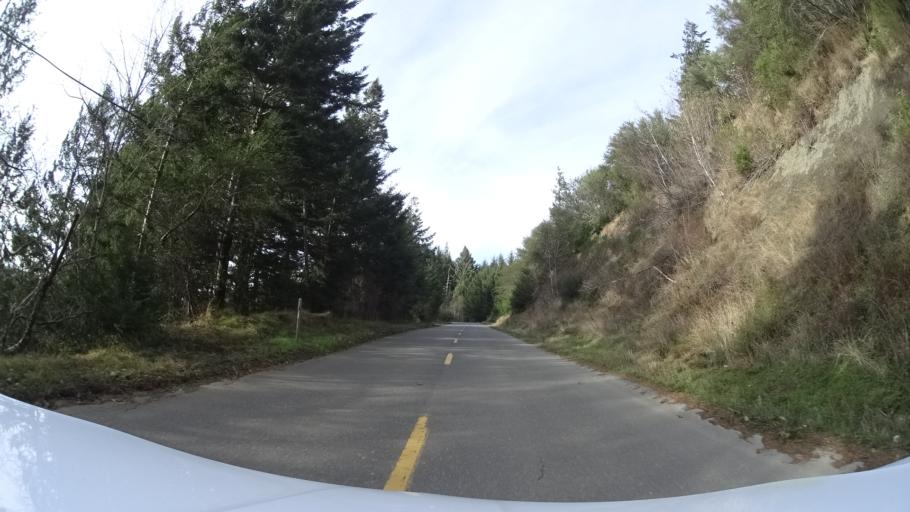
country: US
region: California
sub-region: Humboldt County
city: Ferndale
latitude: 40.5329
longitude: -124.2687
